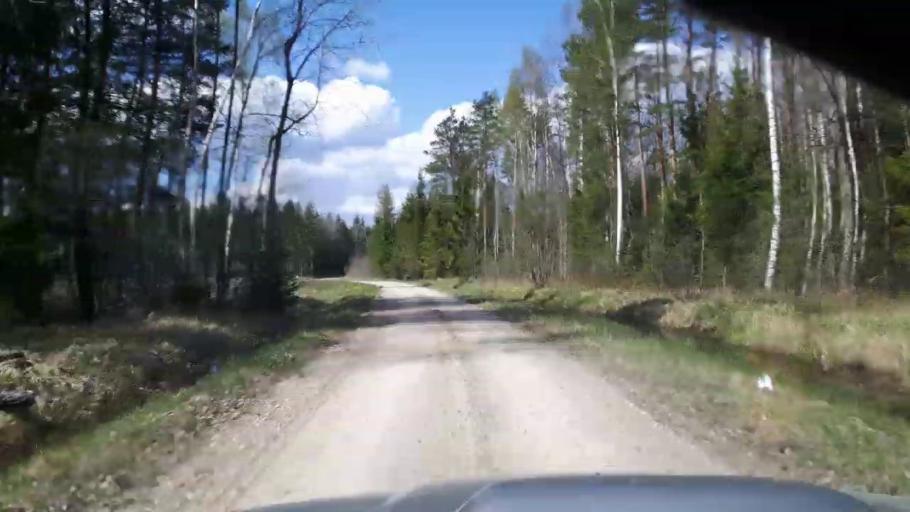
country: EE
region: Paernumaa
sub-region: Tootsi vald
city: Tootsi
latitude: 58.4536
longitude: 24.8903
